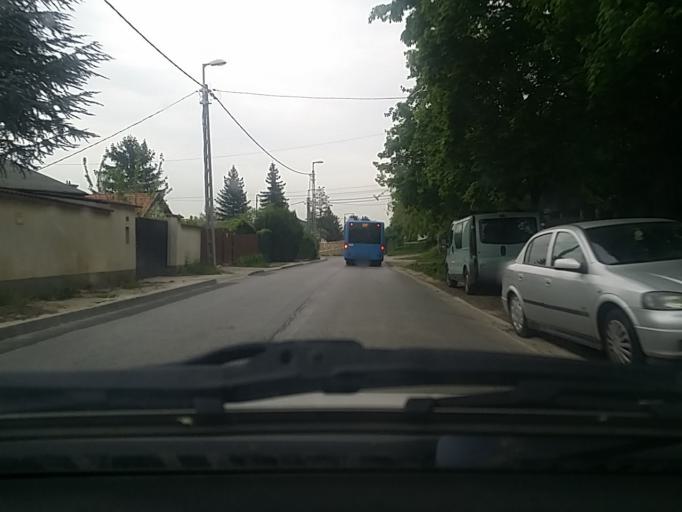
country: HU
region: Budapest
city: Budapest III. keruelet
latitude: 47.5581
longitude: 19.0147
